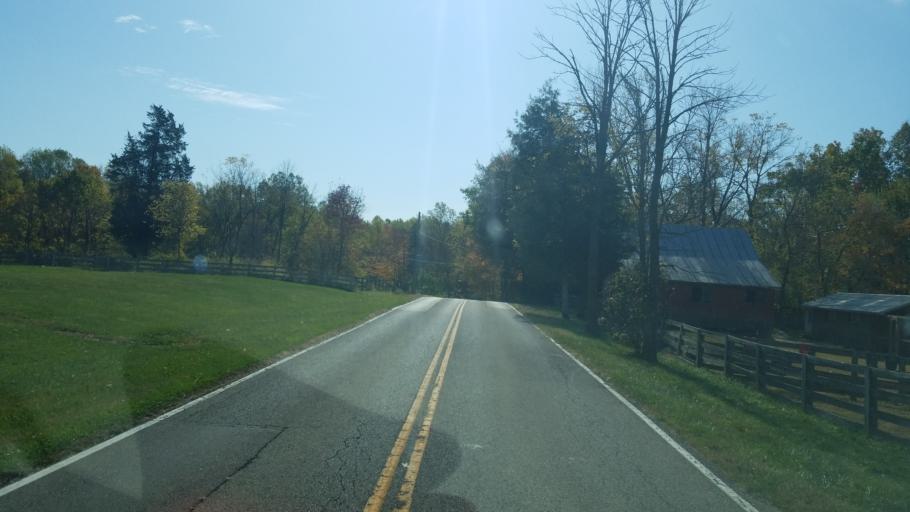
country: US
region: Ohio
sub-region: Warren County
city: Morrow
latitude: 39.4215
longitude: -84.0856
